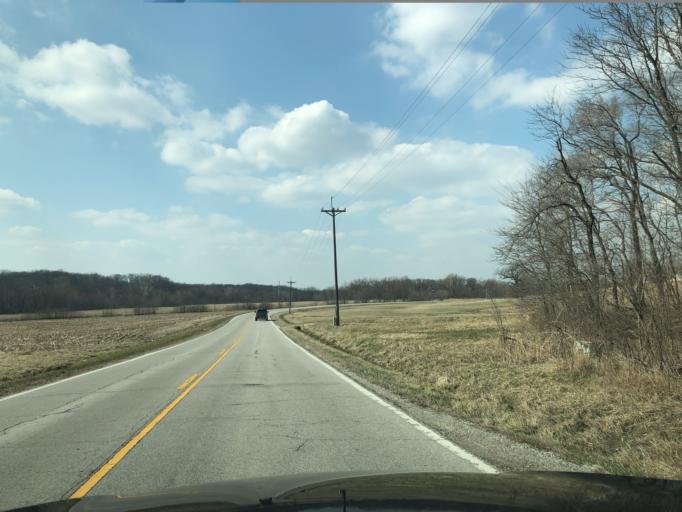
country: US
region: Missouri
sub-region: Platte County
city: Platte City
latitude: 39.4690
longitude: -94.8079
